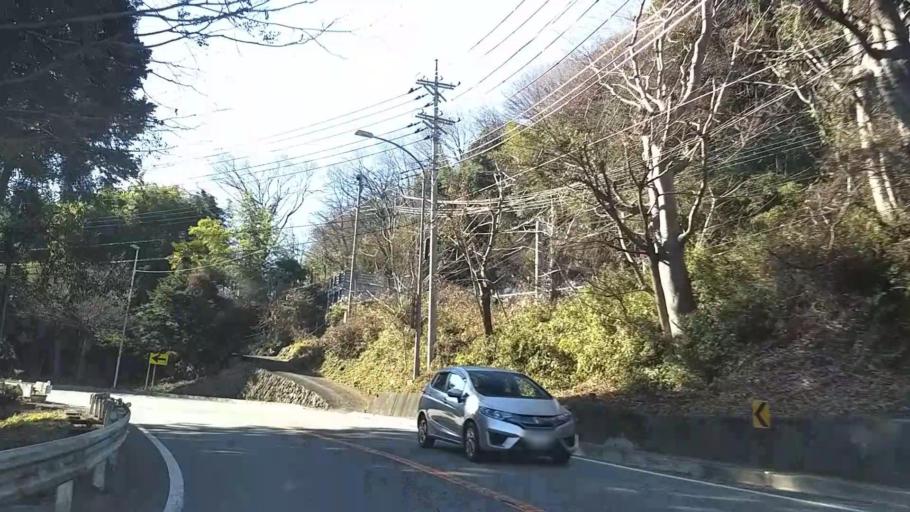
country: JP
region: Yamanashi
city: Uenohara
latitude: 35.6072
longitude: 139.0301
